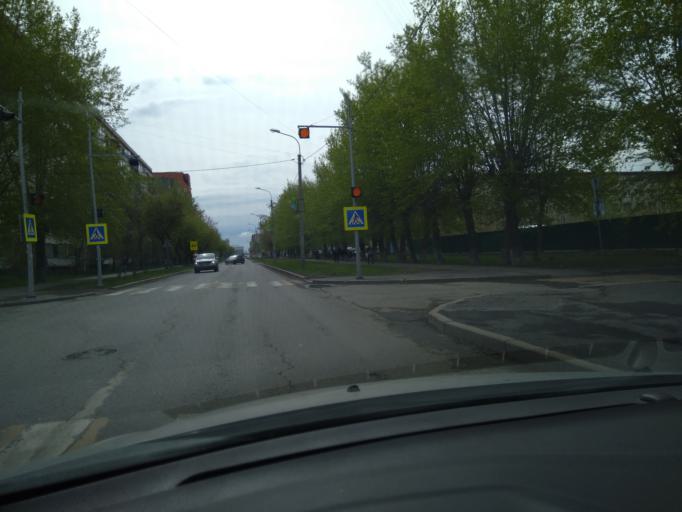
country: RU
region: Tjumen
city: Tyumen
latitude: 57.1383
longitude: 65.5896
